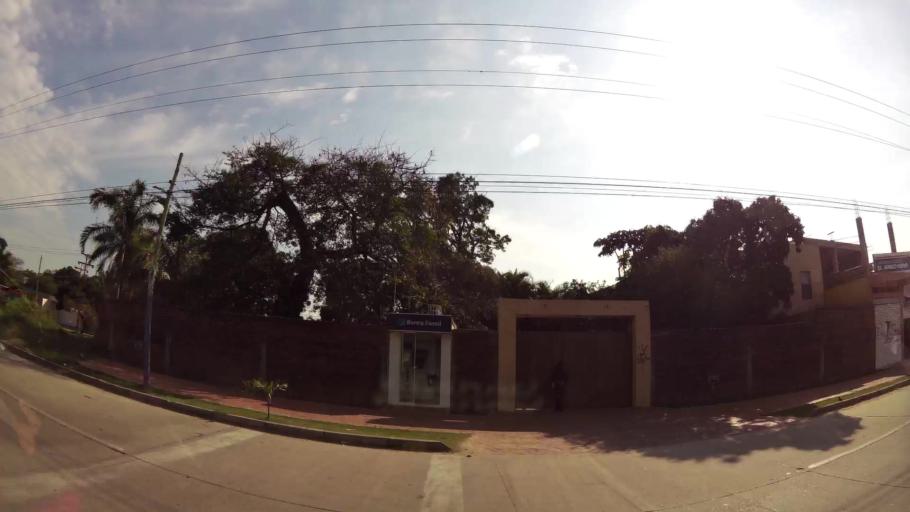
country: BO
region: Santa Cruz
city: Santa Cruz de la Sierra
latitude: -17.7332
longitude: -63.1646
